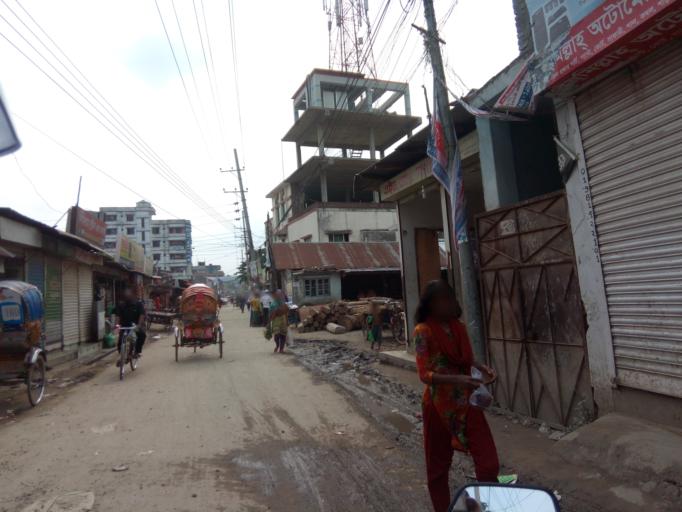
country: BD
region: Dhaka
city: Paltan
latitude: 23.7447
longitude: 90.4483
